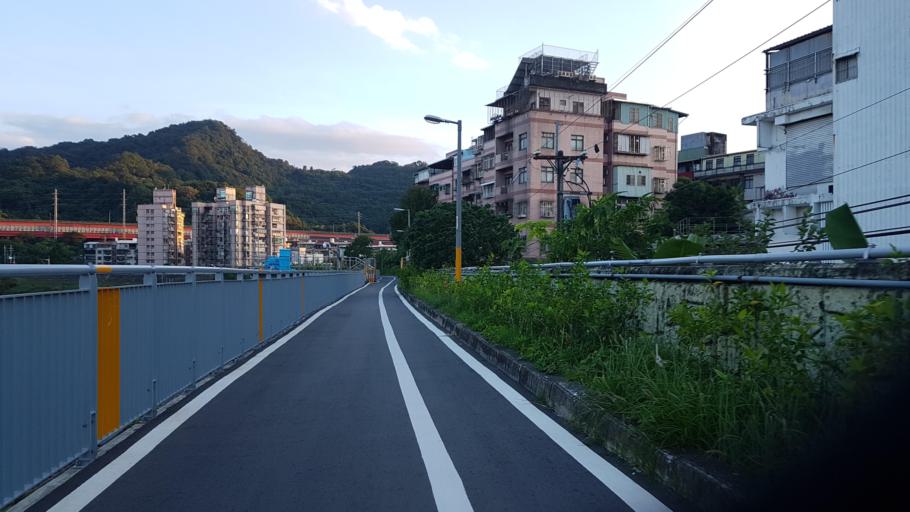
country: TW
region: Taipei
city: Taipei
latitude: 24.9785
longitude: 121.5531
